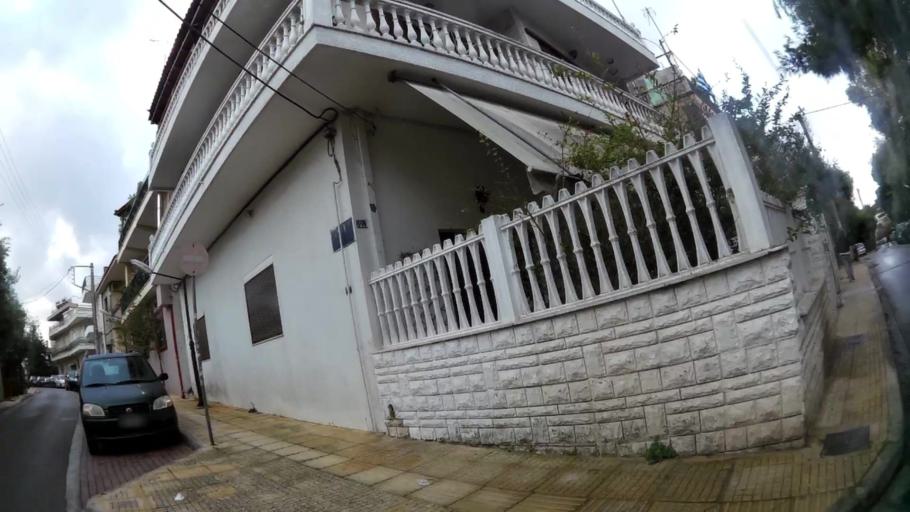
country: GR
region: Attica
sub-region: Nomarchia Athinas
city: Melissia
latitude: 38.0479
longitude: 23.8349
